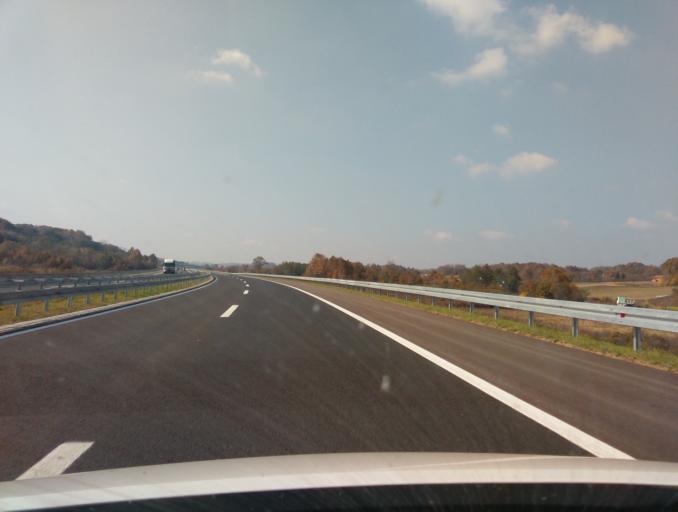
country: BA
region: Republika Srpska
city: Prnjavor
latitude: 44.8946
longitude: 17.5973
